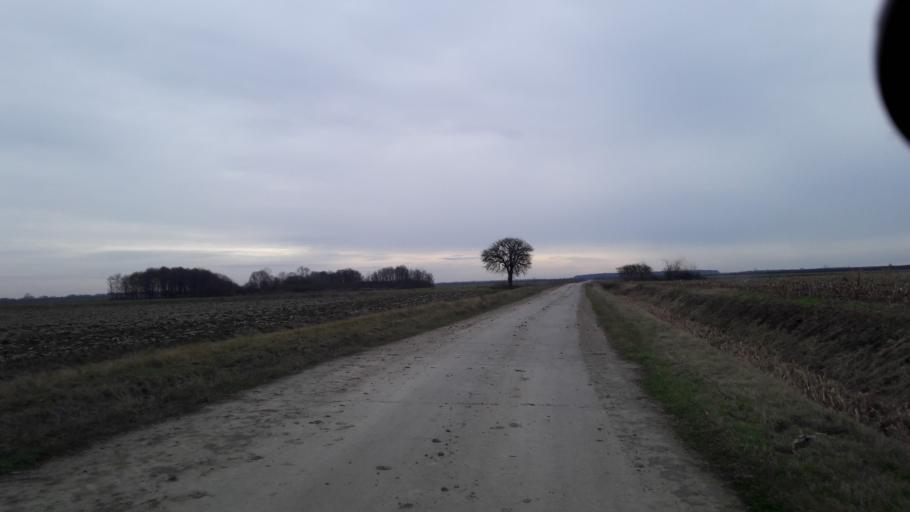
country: HR
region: Osjecko-Baranjska
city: Vladislavci
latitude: 45.4445
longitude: 18.5636
